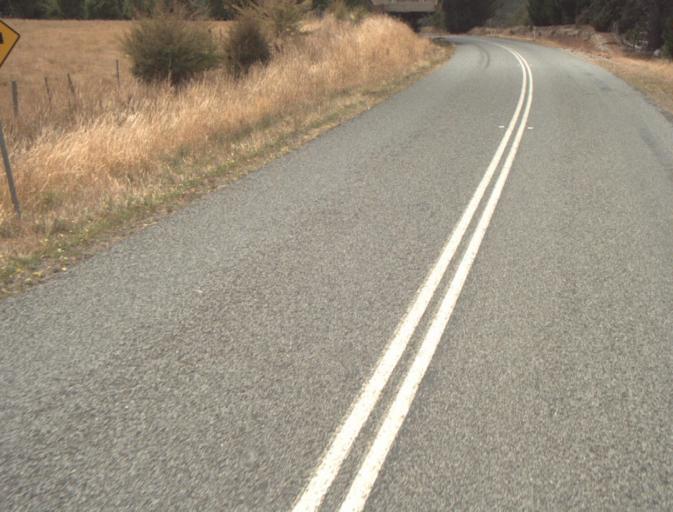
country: AU
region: Tasmania
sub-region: Northern Midlands
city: Evandale
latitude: -41.5044
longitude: 147.4802
